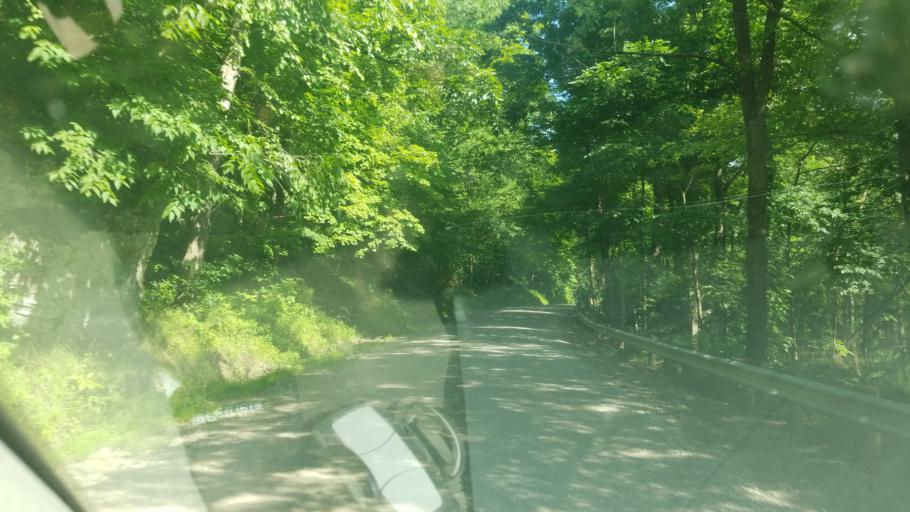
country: US
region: Ohio
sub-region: Holmes County
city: Millersburg
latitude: 40.4206
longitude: -81.9510
